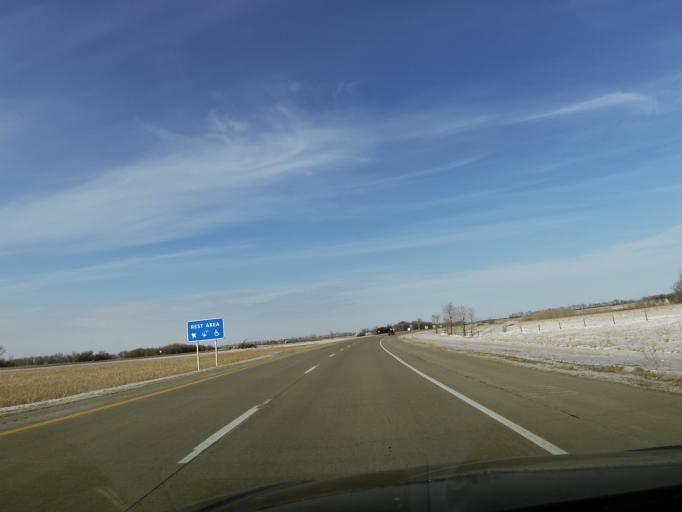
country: US
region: North Dakota
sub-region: Walsh County
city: Grafton
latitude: 48.4530
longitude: -97.1944
